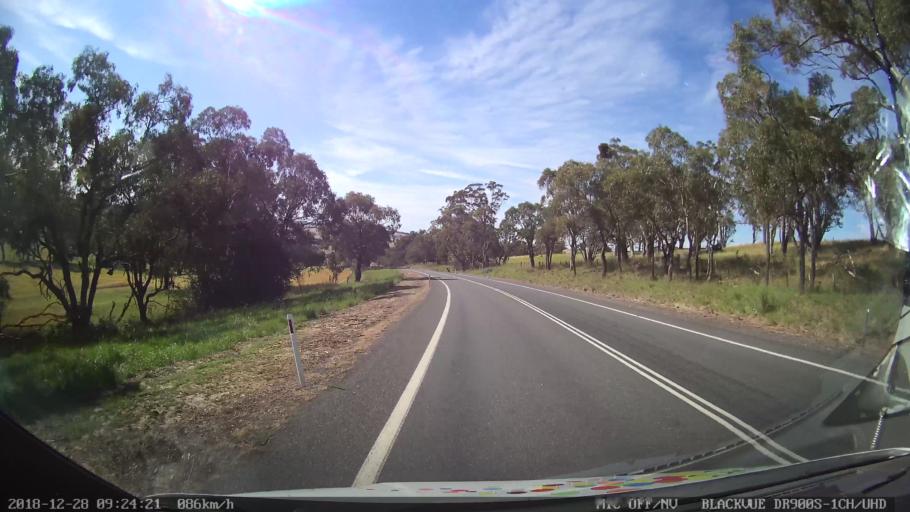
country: AU
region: New South Wales
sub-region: Upper Lachlan Shire
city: Crookwell
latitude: -34.3966
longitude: 149.3803
